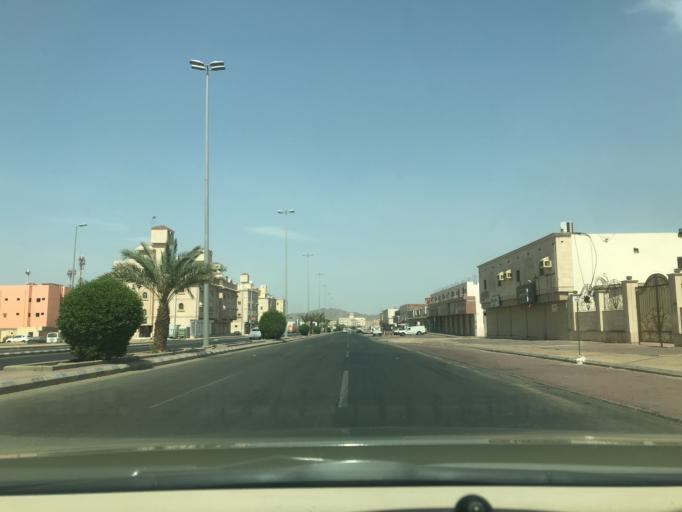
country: SA
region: Makkah
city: Al Jumum
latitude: 21.6245
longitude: 39.6720
